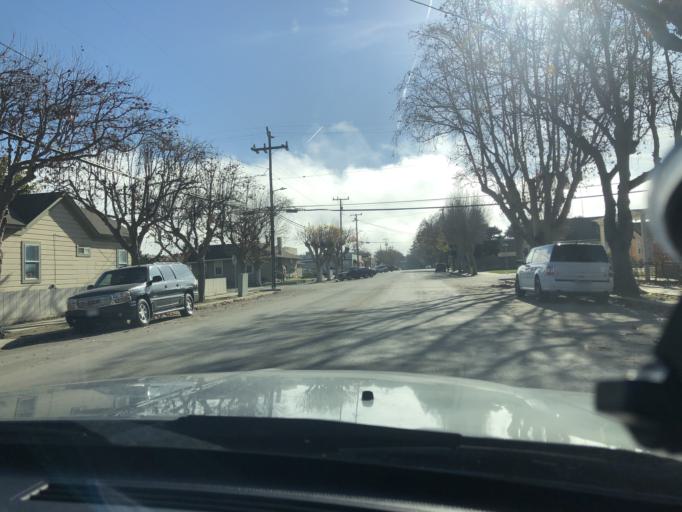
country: US
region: California
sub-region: Monterey County
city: King City
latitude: 36.2127
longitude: -121.1300
